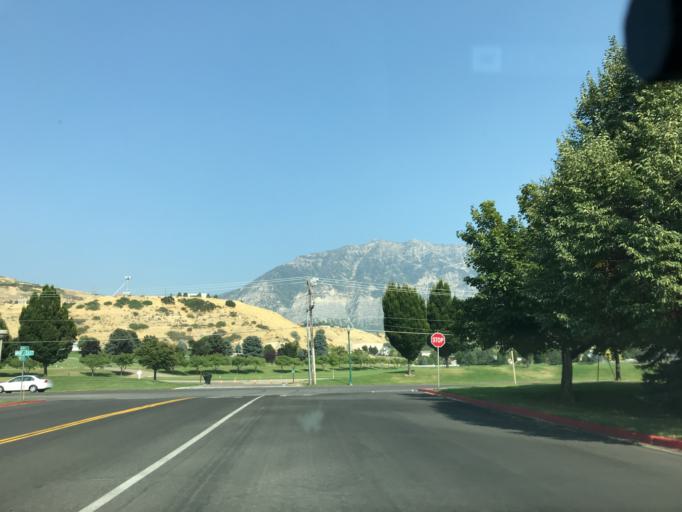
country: US
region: Utah
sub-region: Utah County
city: Orem
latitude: 40.3214
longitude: -111.6774
